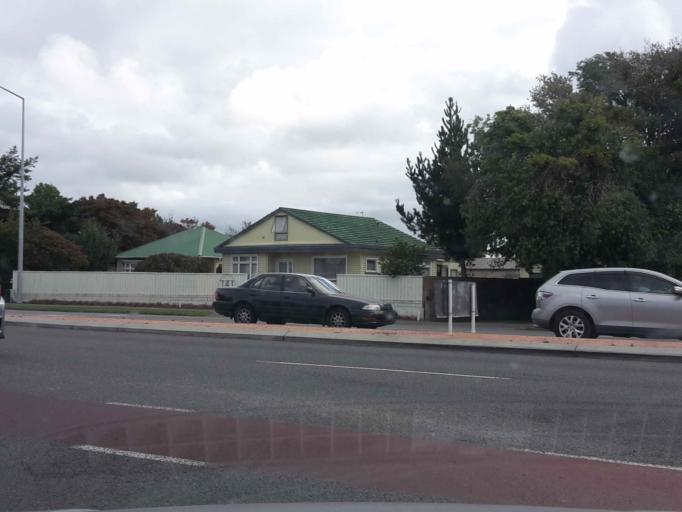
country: NZ
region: Canterbury
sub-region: Christchurch City
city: Christchurch
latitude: -43.4880
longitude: 172.6161
